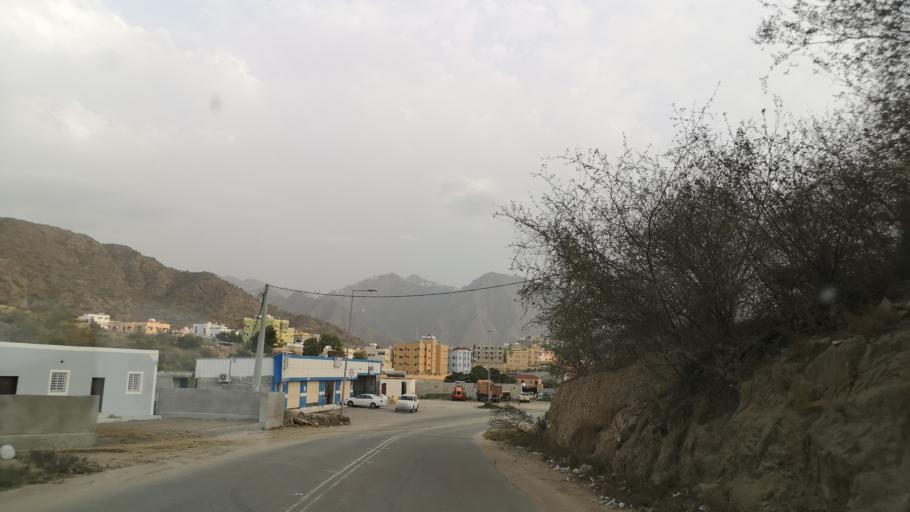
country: YE
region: Sa'dah
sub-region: Monabbih
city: Suq al Khamis
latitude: 17.3590
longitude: 43.1296
